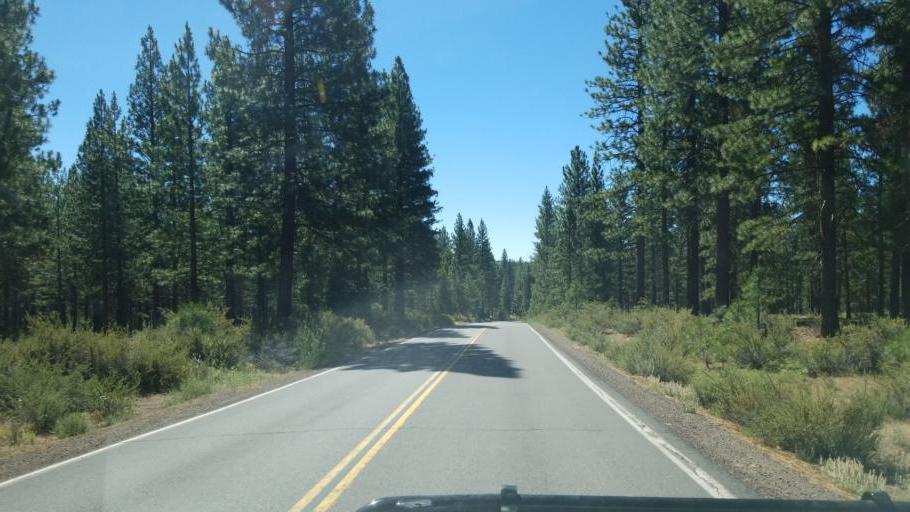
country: US
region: California
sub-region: Lassen County
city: Susanville
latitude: 40.4298
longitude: -120.7294
